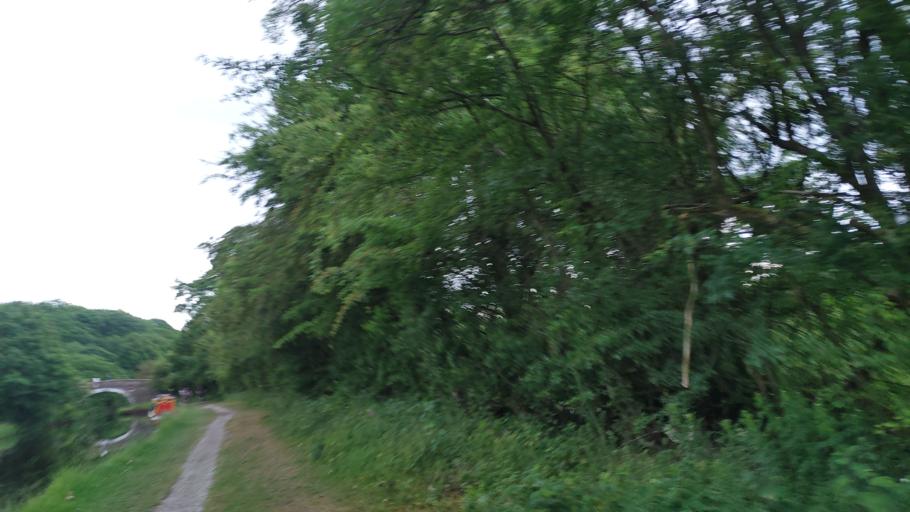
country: GB
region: England
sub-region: Lancashire
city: Chorley
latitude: 53.6928
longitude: -2.6053
